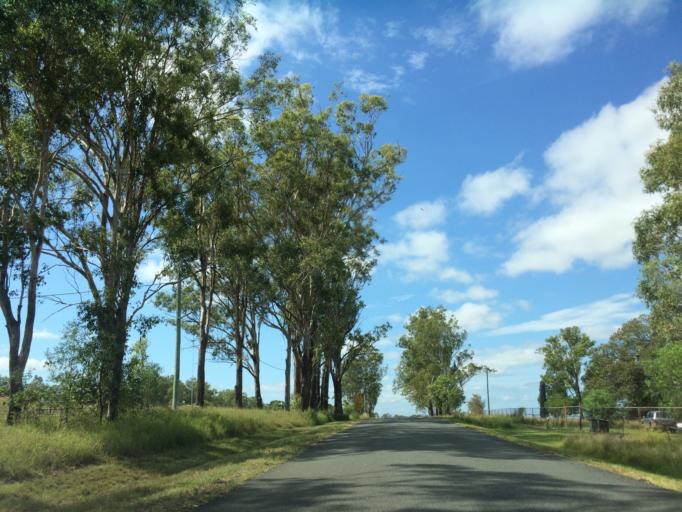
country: AU
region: Queensland
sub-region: Logan
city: Cedar Vale
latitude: -27.8856
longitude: 152.9724
